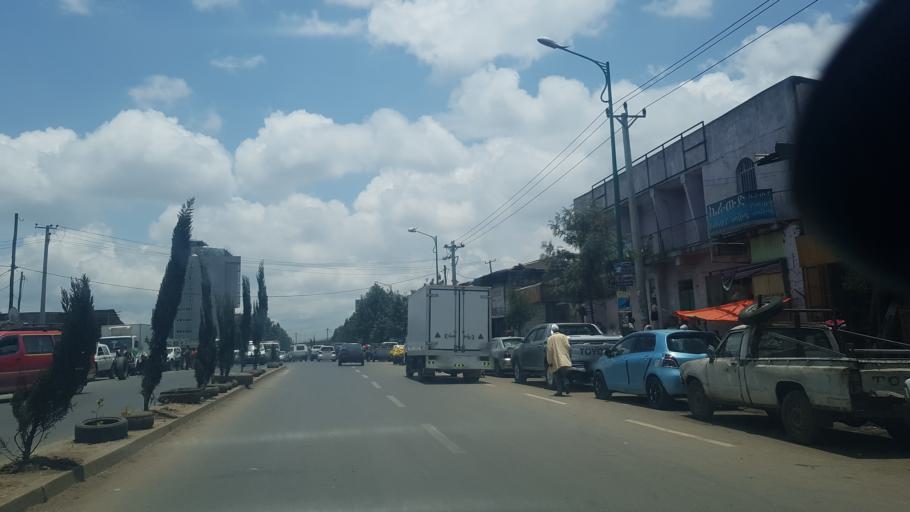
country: ET
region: Adis Abeba
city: Addis Ababa
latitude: 9.0232
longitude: 38.7360
